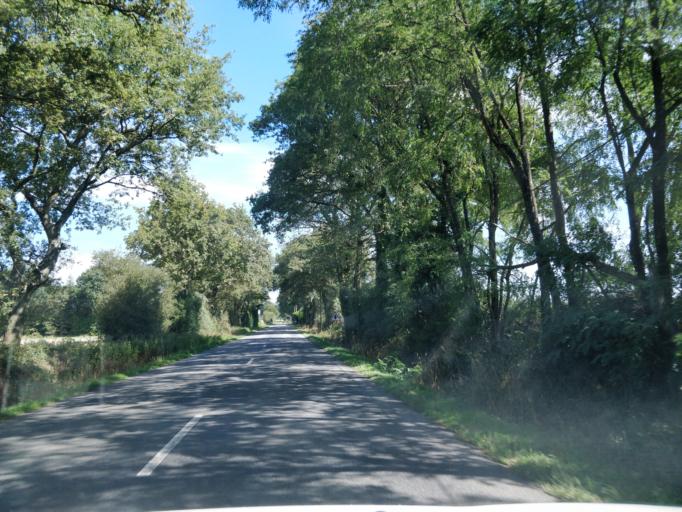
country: FR
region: Pays de la Loire
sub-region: Departement de la Loire-Atlantique
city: Guemene-Penfao
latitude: 47.6396
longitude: -1.8034
